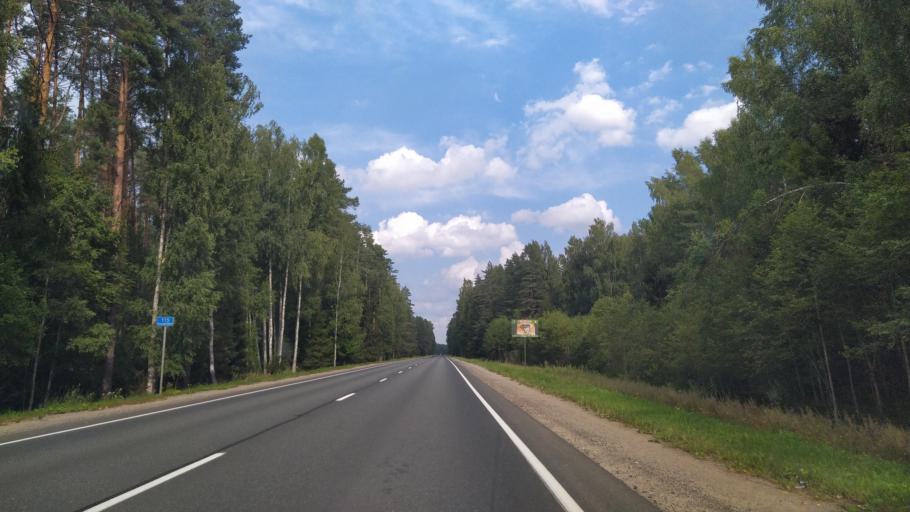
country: RU
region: Pskov
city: Dno
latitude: 57.9865
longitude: 29.8103
